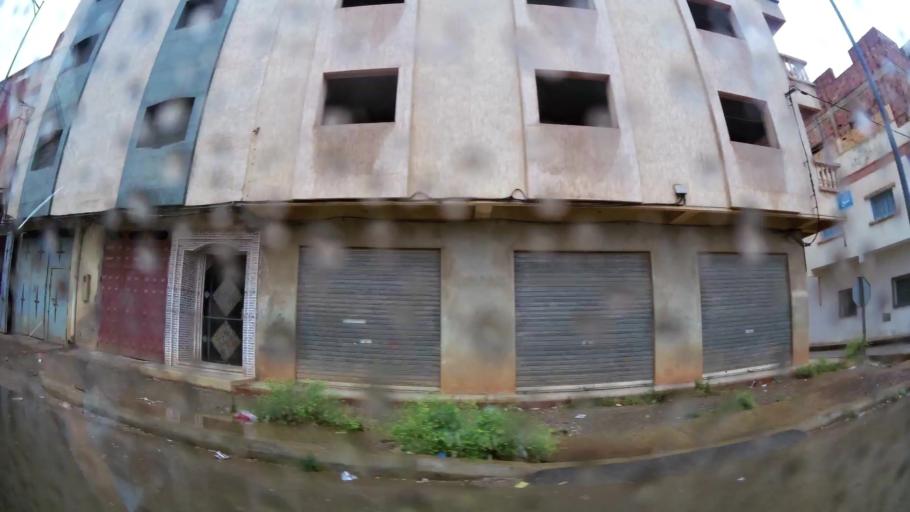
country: MA
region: Oriental
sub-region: Nador
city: Boudinar
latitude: 35.1149
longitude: -3.6437
